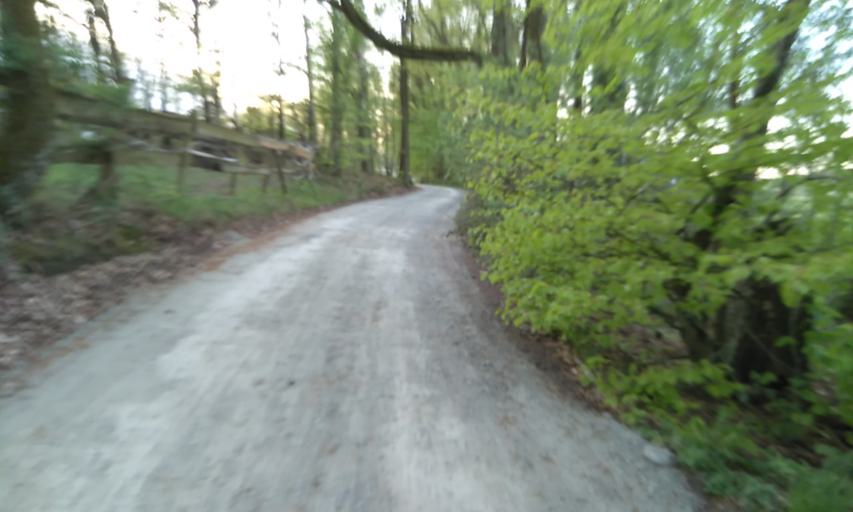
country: DE
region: Lower Saxony
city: Nottensdorf
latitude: 53.4924
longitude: 9.6145
